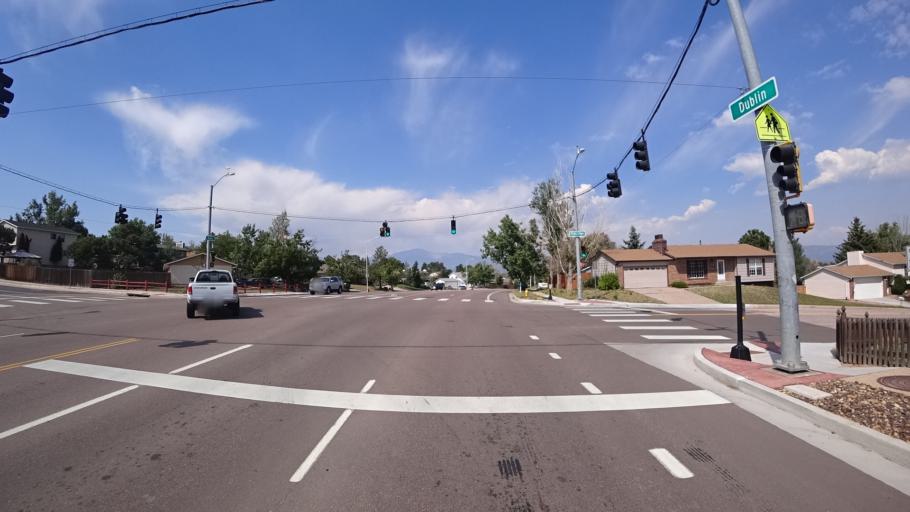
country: US
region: Colorado
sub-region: El Paso County
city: Cimarron Hills
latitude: 38.9250
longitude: -104.7676
